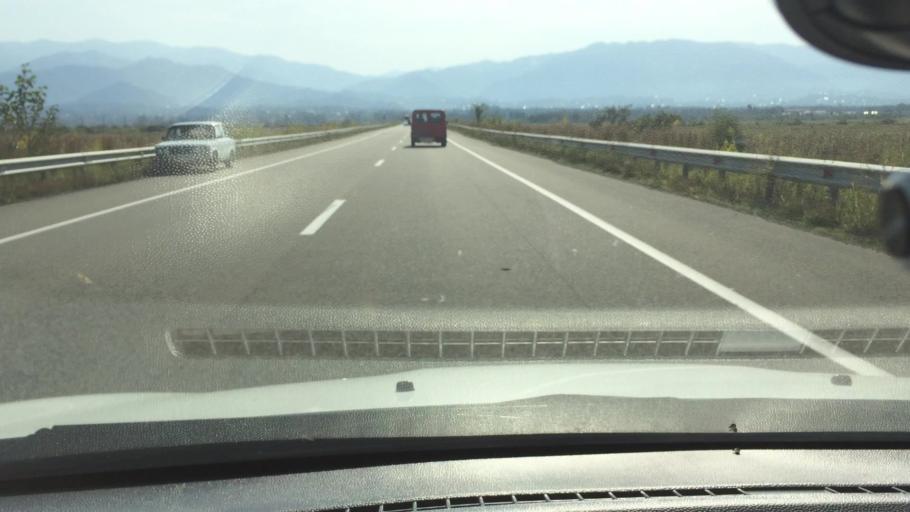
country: GE
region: Ajaria
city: Ochkhamuri
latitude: 41.8750
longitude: 41.8260
